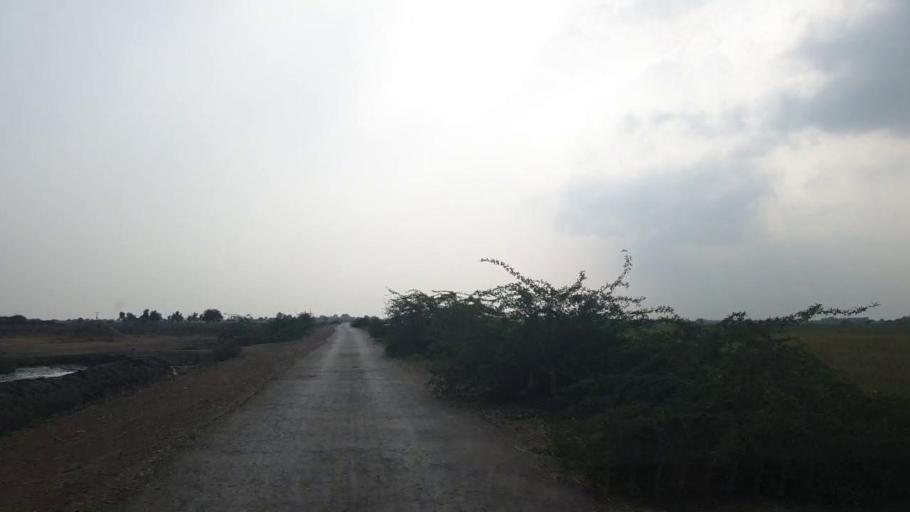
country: PK
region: Sindh
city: Badin
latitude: 24.6502
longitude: 68.6996
